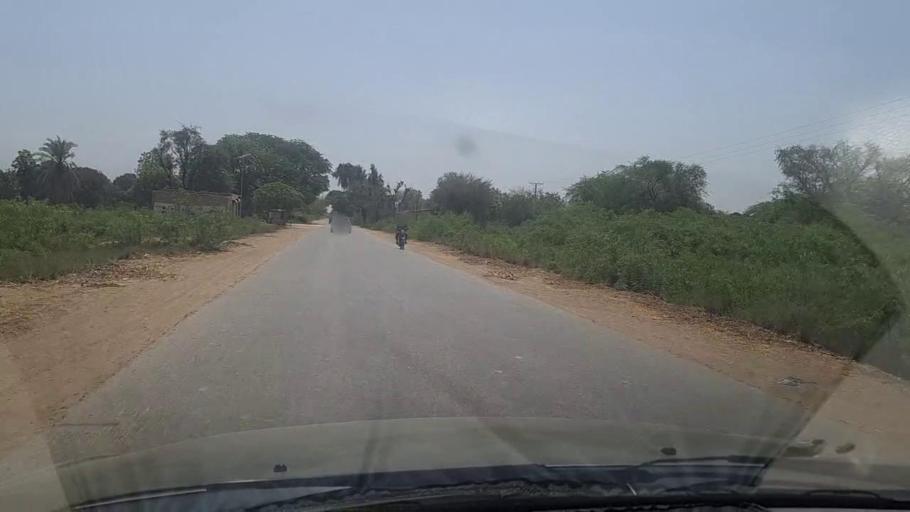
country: PK
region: Sindh
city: Tando Jam
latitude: 25.3045
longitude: 68.5802
